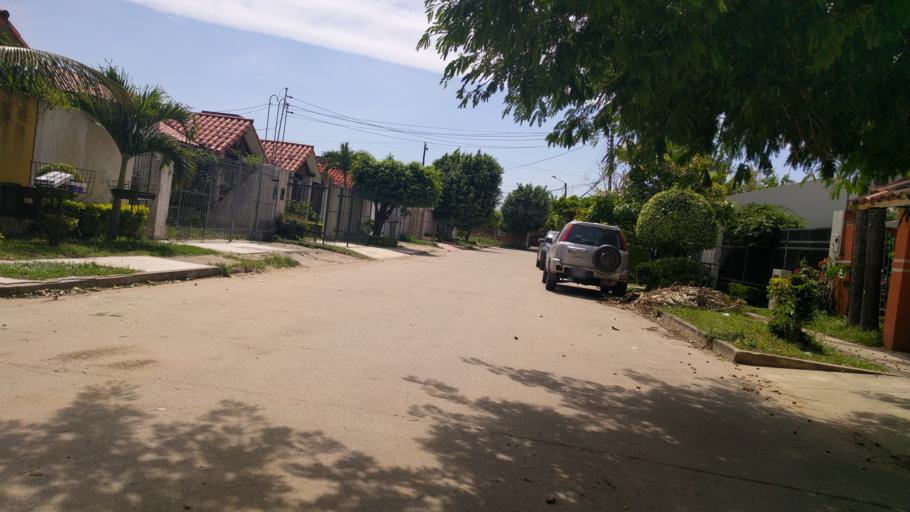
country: BO
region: Santa Cruz
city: Santa Cruz de la Sierra
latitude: -17.8184
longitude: -63.2204
